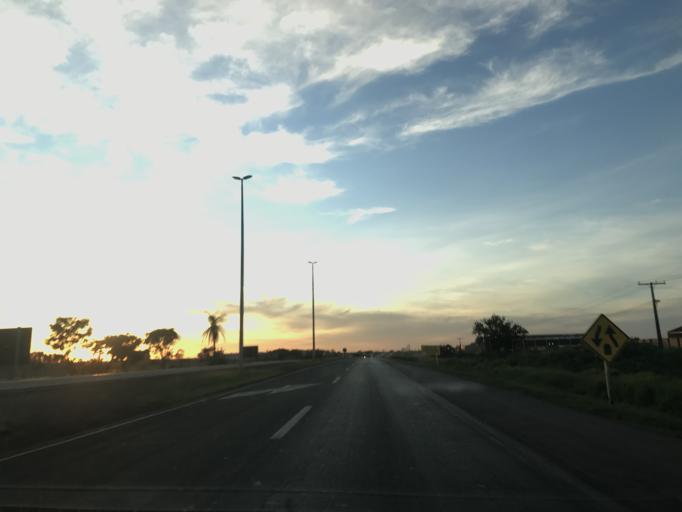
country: BR
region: Goias
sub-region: Luziania
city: Luziania
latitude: -16.2485
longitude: -47.9039
